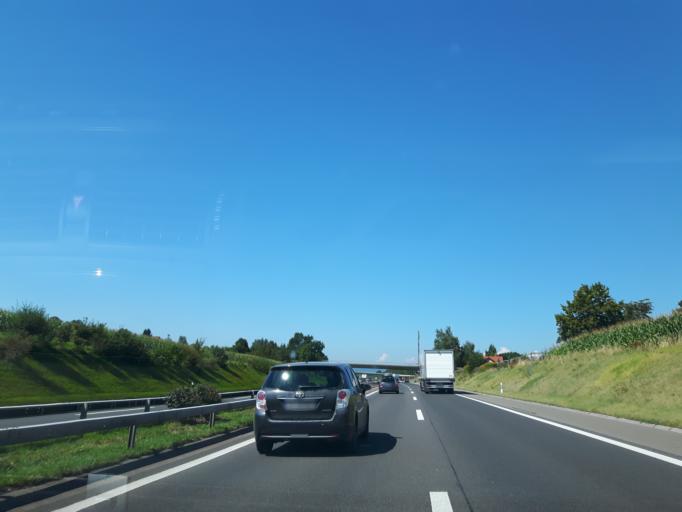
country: CH
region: Zurich
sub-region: Bezirk Horgen
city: Waedenswil / Leihof-Muehlebach
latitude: 47.2177
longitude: 8.6659
